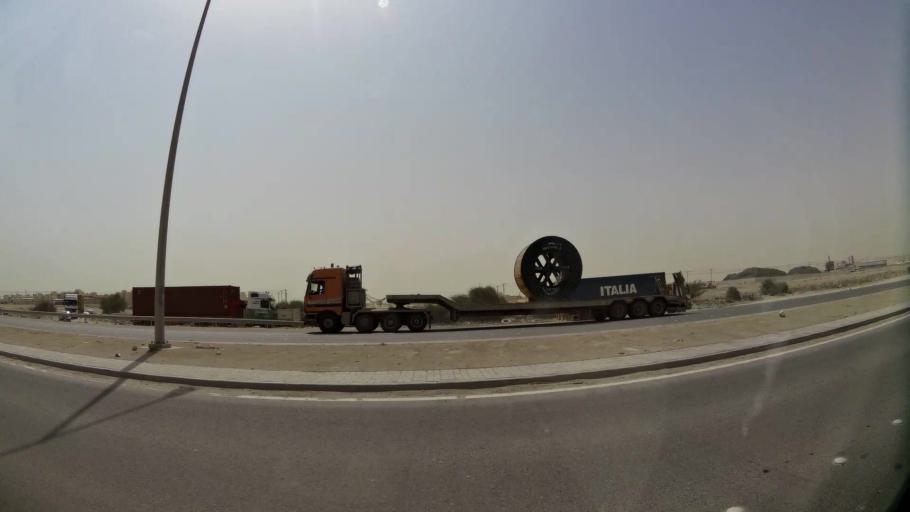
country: QA
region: Baladiyat ar Rayyan
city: Ar Rayyan
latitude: 25.1805
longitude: 51.4123
